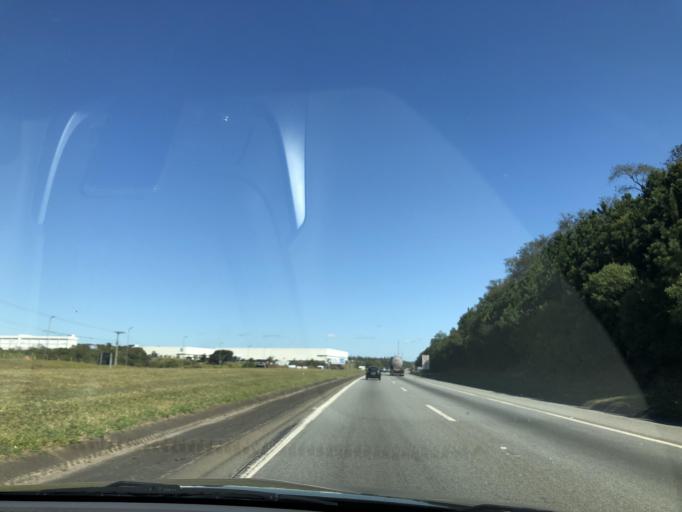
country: BR
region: Sao Paulo
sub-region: Sorocaba
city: Sorocaba
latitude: -23.4150
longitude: -47.3451
